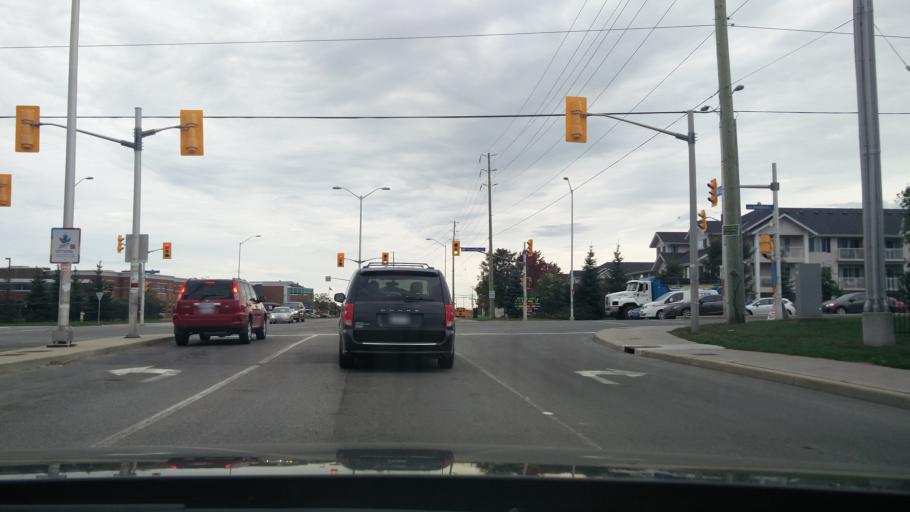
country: CA
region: Ontario
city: Bells Corners
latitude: 45.2743
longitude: -75.7388
